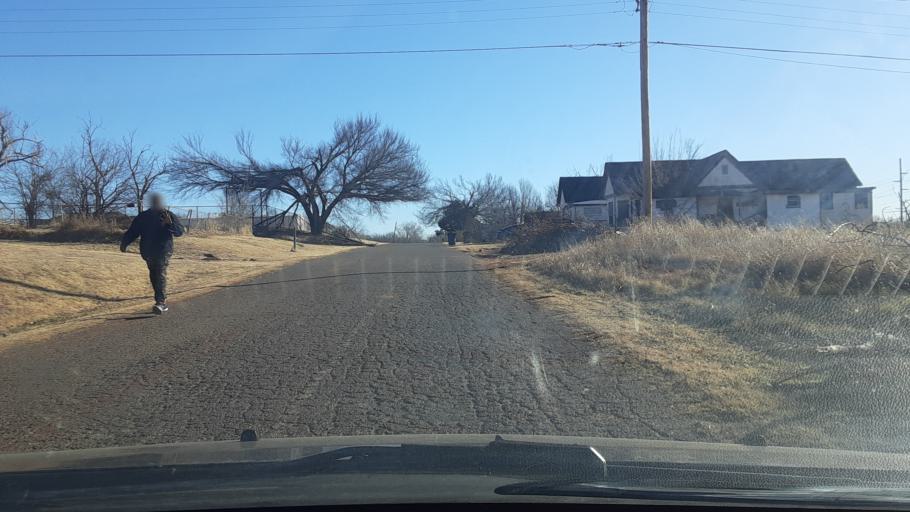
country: US
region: Oklahoma
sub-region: Logan County
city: Guthrie
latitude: 35.8729
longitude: -97.4147
